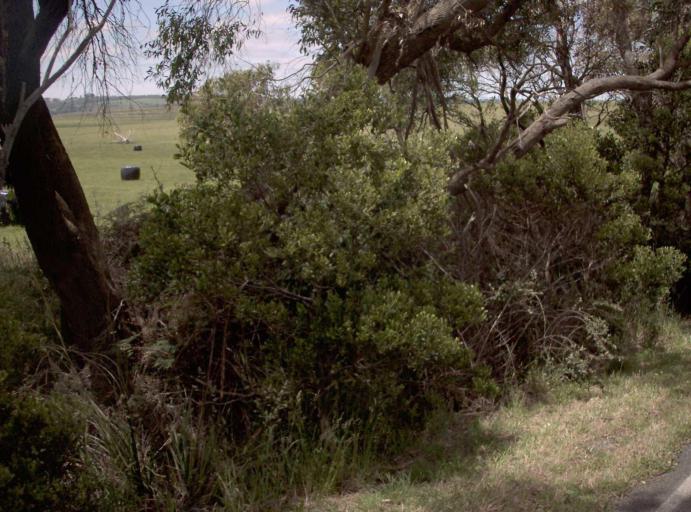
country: AU
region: Victoria
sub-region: Bass Coast
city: North Wonthaggi
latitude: -38.6127
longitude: 146.0166
